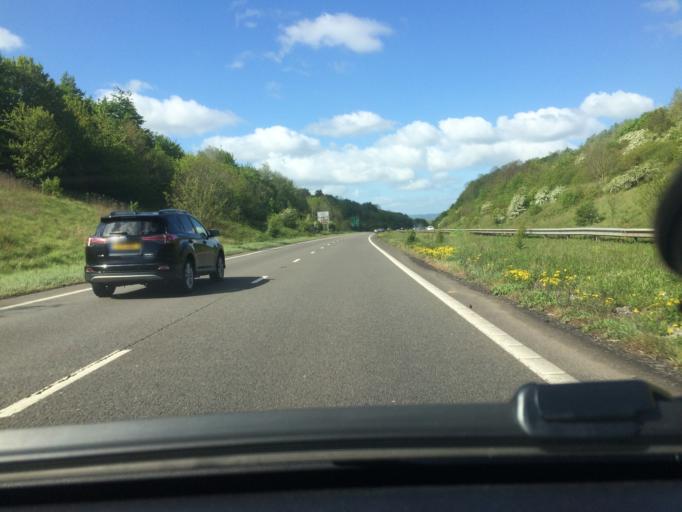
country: GB
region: England
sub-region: Cheshire West and Chester
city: Eccleston
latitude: 53.1591
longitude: -2.8889
